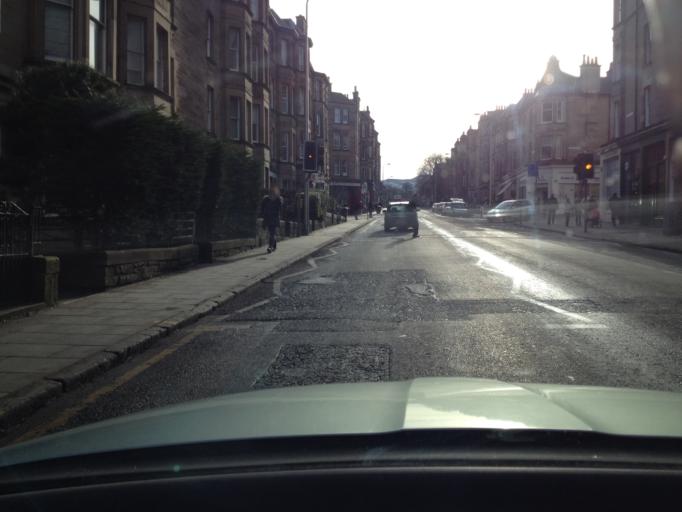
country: GB
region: Scotland
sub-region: Edinburgh
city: Edinburgh
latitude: 55.9230
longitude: -3.2107
